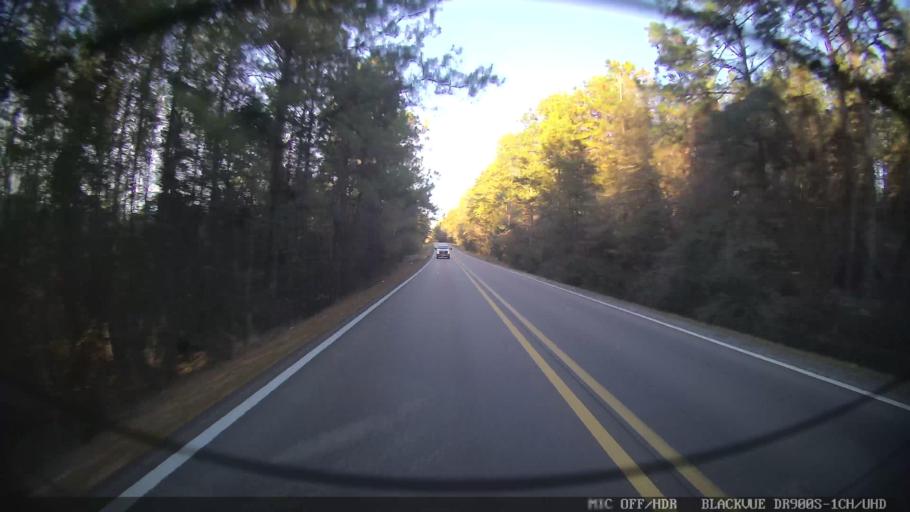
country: US
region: Mississippi
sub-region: Lamar County
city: Lumberton
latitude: 31.0601
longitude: -89.4266
